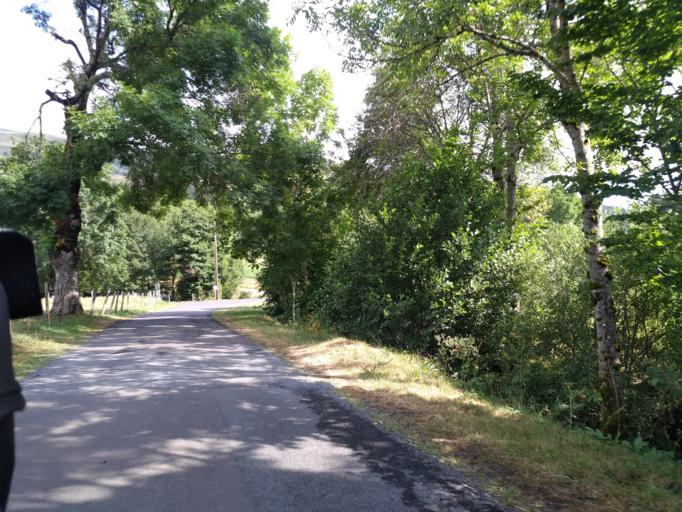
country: FR
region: Auvergne
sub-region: Departement du Cantal
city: Murat
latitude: 45.1340
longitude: 2.7454
